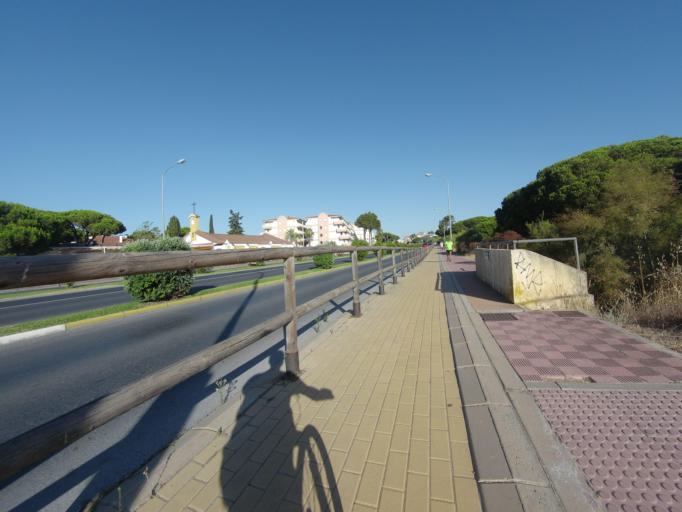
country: ES
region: Andalusia
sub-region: Provincia de Huelva
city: Aljaraque
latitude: 37.2107
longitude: -7.0434
